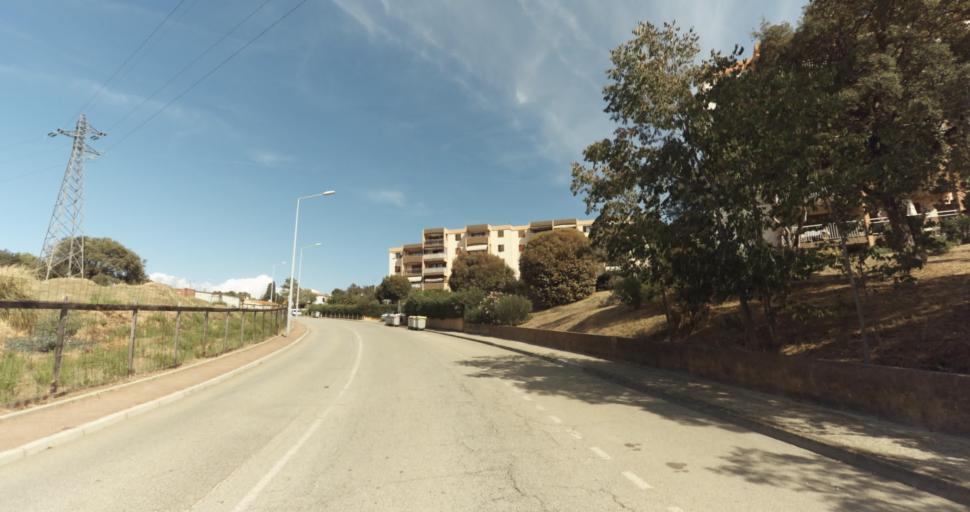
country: FR
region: Corsica
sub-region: Departement de la Corse-du-Sud
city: Ajaccio
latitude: 41.9377
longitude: 8.7624
